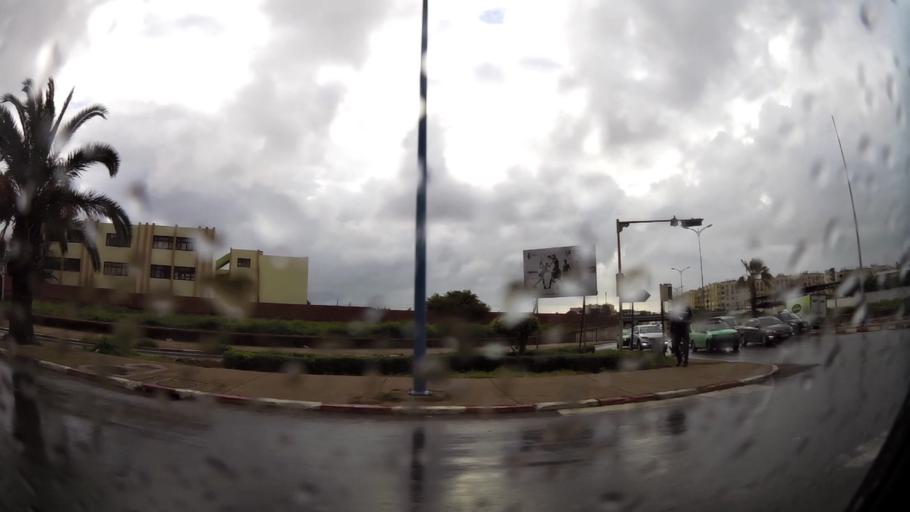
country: MA
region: Grand Casablanca
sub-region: Mohammedia
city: Mohammedia
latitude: 33.6767
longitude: -7.3965
